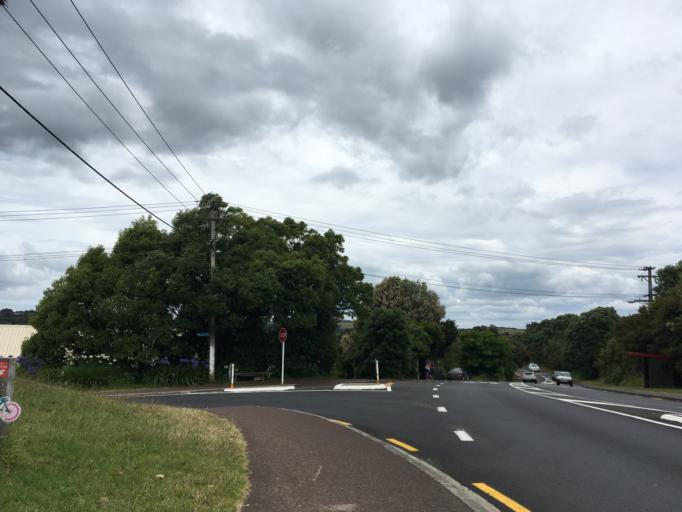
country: NZ
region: Auckland
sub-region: Auckland
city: Pakuranga
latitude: -36.7965
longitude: 175.0323
